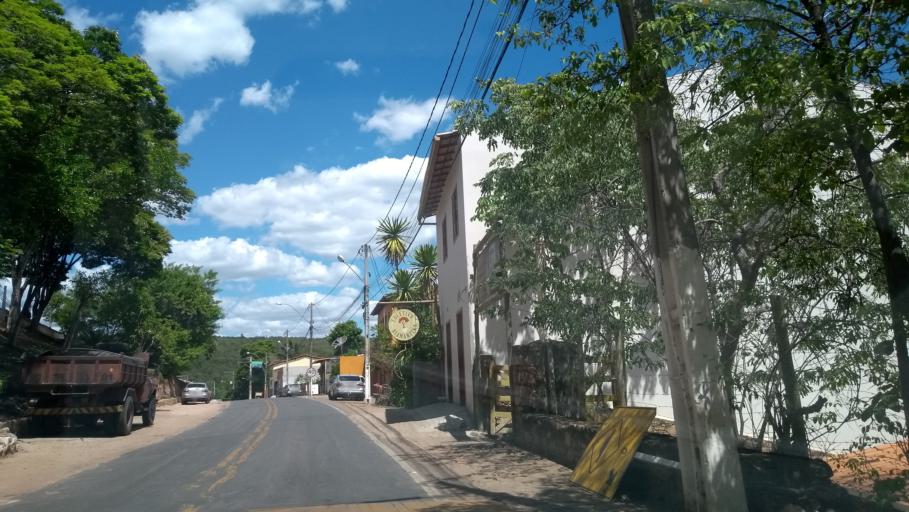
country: BR
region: Bahia
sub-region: Andarai
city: Vera Cruz
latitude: -12.5609
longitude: -41.3872
